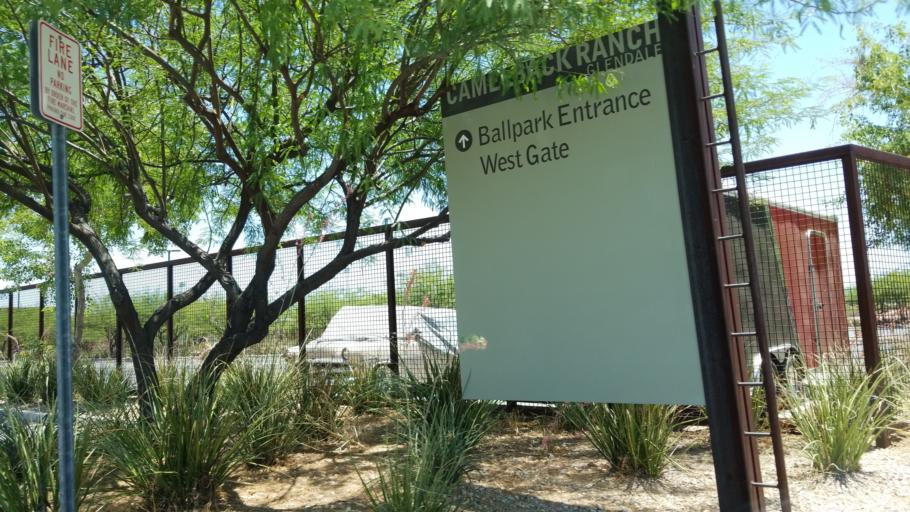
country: US
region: Arizona
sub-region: Maricopa County
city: Litchfield Park
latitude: 33.5134
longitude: -112.2983
